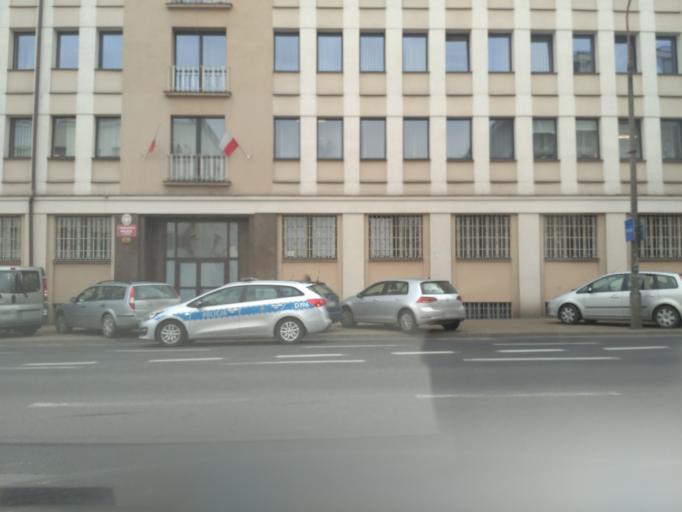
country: PL
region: Lublin Voivodeship
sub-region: Powiat lubelski
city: Lublin
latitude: 51.2453
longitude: 22.5567
